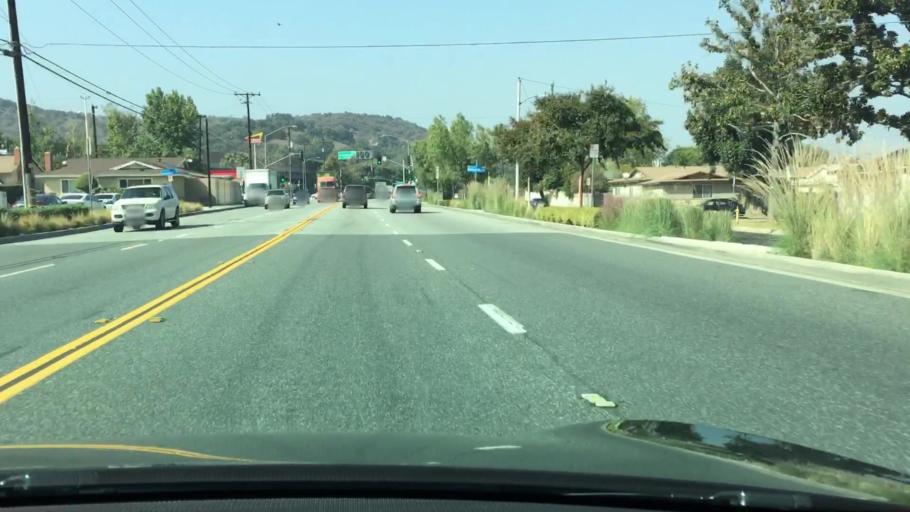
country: US
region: California
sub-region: Los Angeles County
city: Avocado Heights
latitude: 34.0190
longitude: -117.9855
